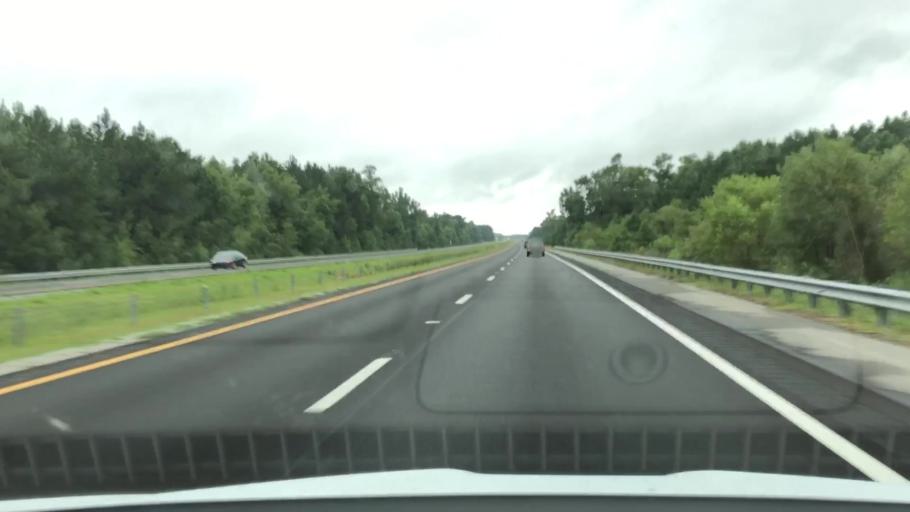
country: US
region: North Carolina
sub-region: Wayne County
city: Goldsboro
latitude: 35.4537
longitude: -77.9845
